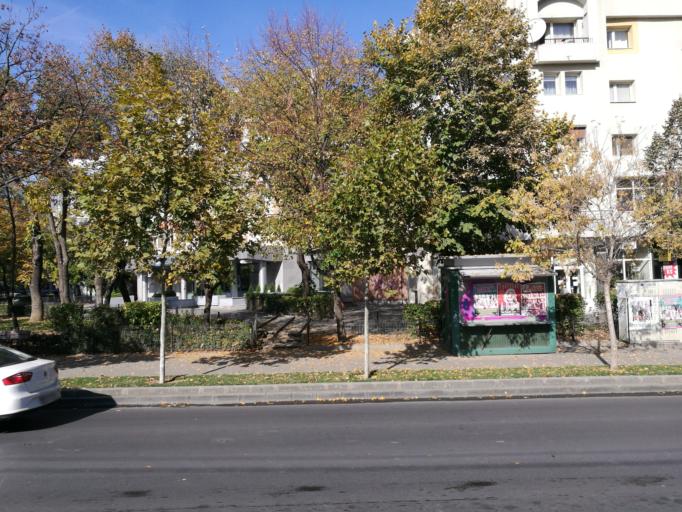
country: RO
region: Bucuresti
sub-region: Municipiul Bucuresti
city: Bucharest
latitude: 44.4791
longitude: 26.0934
